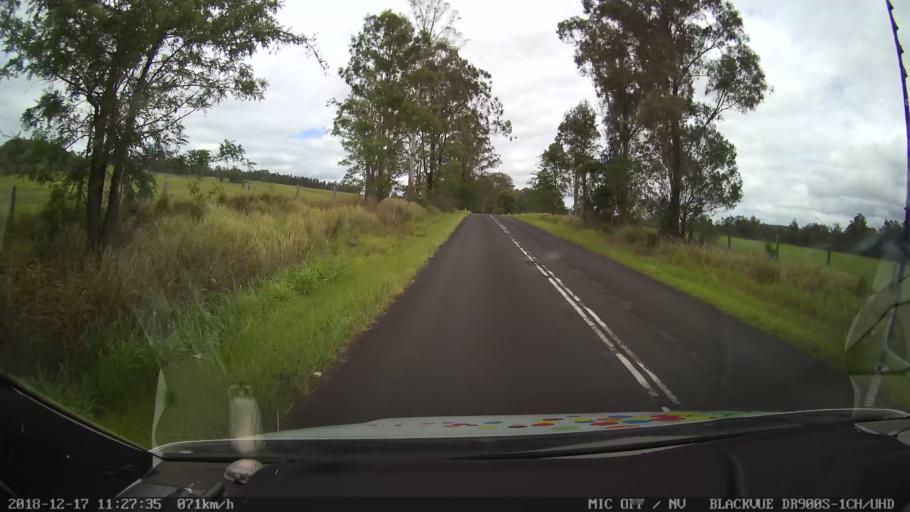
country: AU
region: New South Wales
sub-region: Kyogle
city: Kyogle
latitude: -28.7476
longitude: 152.6453
